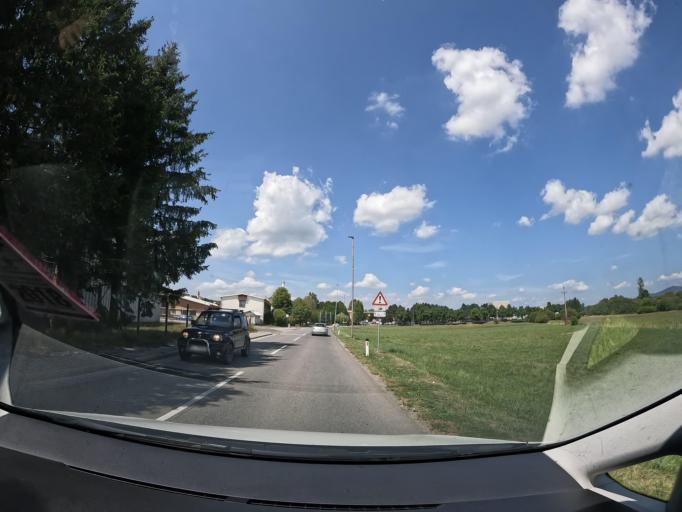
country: SI
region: Pivka
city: Pivka
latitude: 45.6786
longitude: 14.2012
